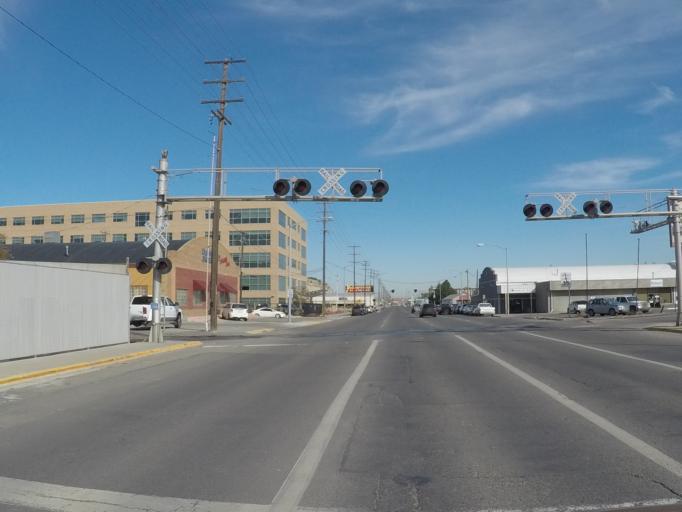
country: US
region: Montana
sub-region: Yellowstone County
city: Billings
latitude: 45.7884
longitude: -108.5007
